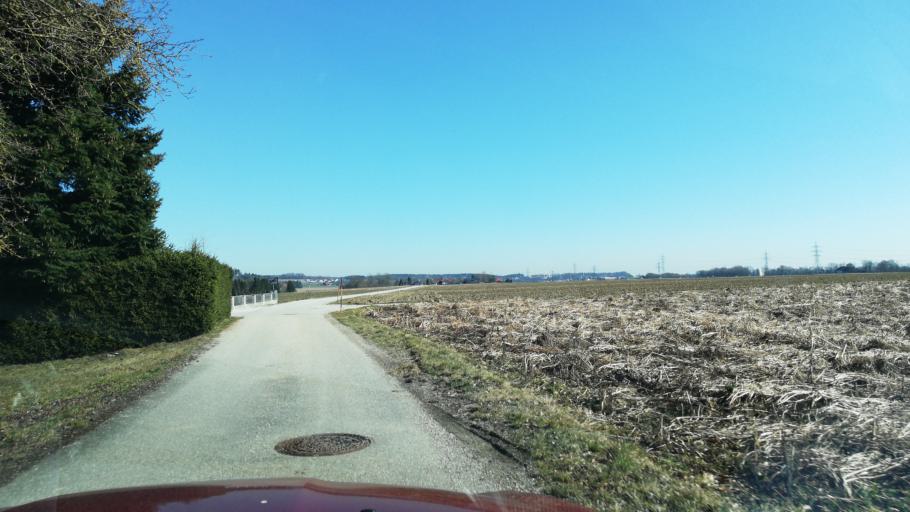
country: AT
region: Upper Austria
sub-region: Wels-Land
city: Neukirchen bei Lambach
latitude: 48.0884
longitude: 13.8235
